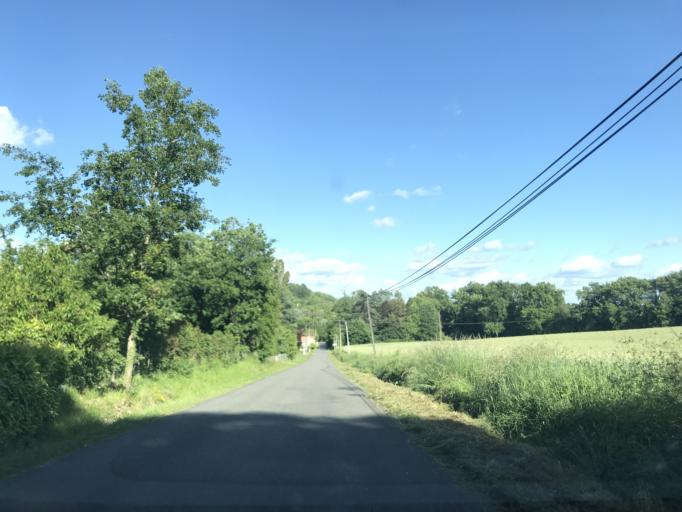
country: FR
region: Poitou-Charentes
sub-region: Departement de la Charente
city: Chalais
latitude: 45.2748
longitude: -0.0117
